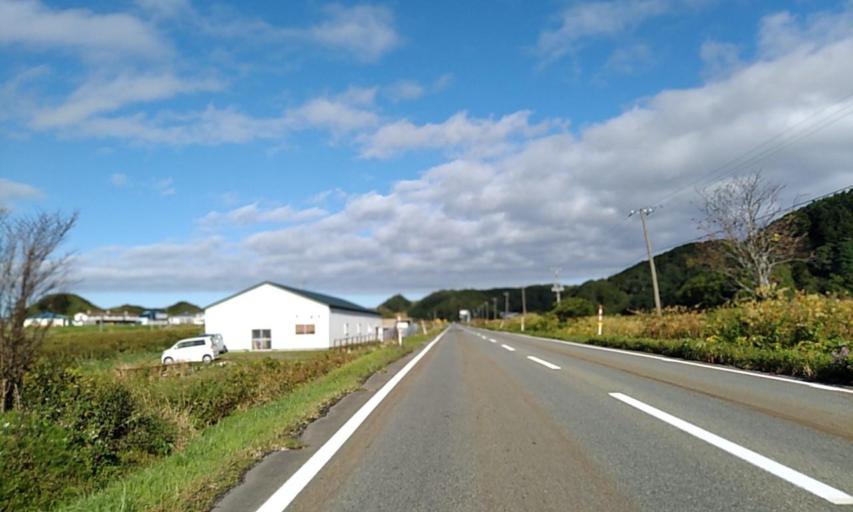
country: JP
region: Hokkaido
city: Shizunai-furukawacho
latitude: 42.2278
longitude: 142.6177
